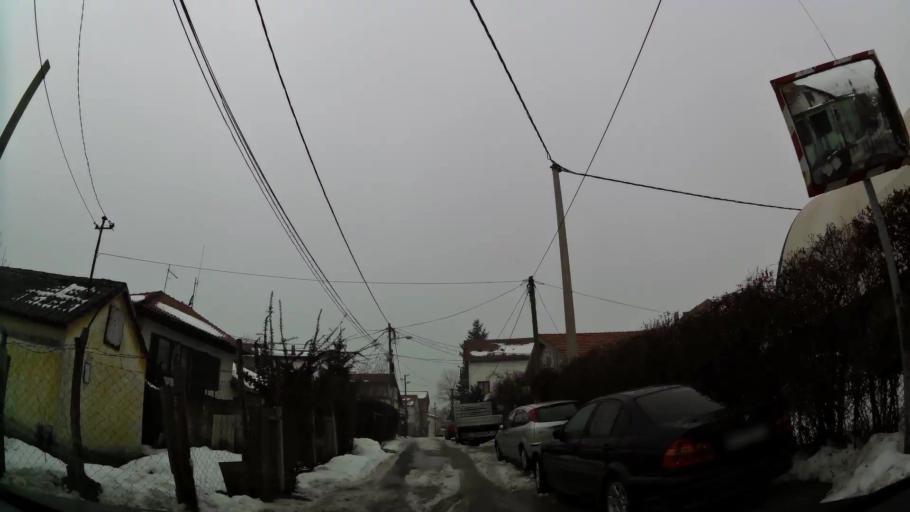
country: RS
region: Central Serbia
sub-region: Belgrade
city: Zvezdara
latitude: 44.7849
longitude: 20.5223
